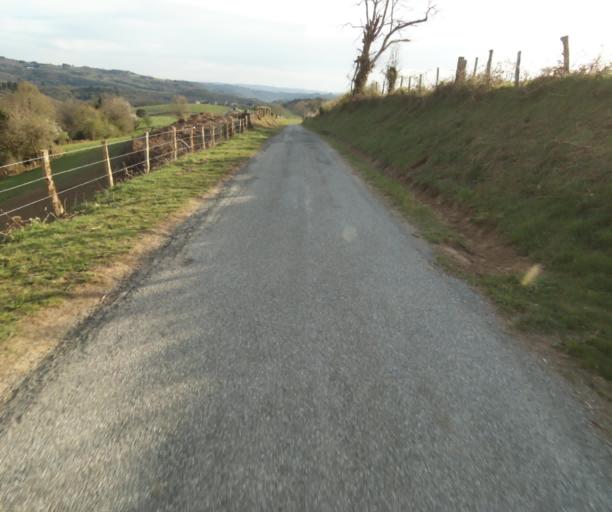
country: FR
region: Limousin
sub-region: Departement de la Correze
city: Correze
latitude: 45.3725
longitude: 1.8345
